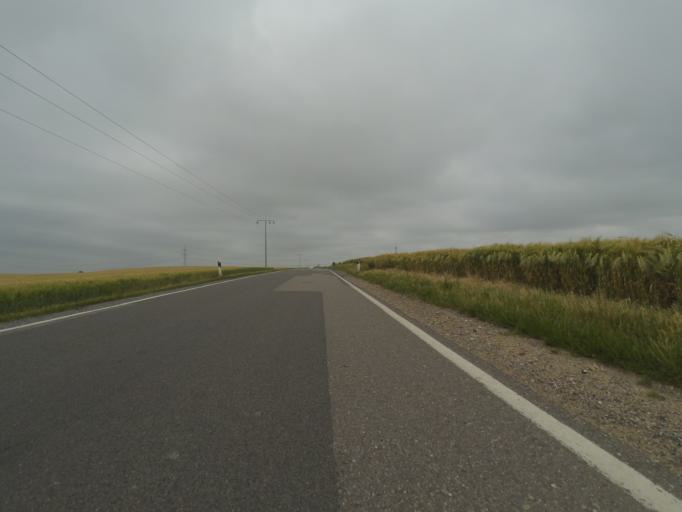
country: DE
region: Mecklenburg-Vorpommern
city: Gaegelow
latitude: 53.6881
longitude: 11.8949
